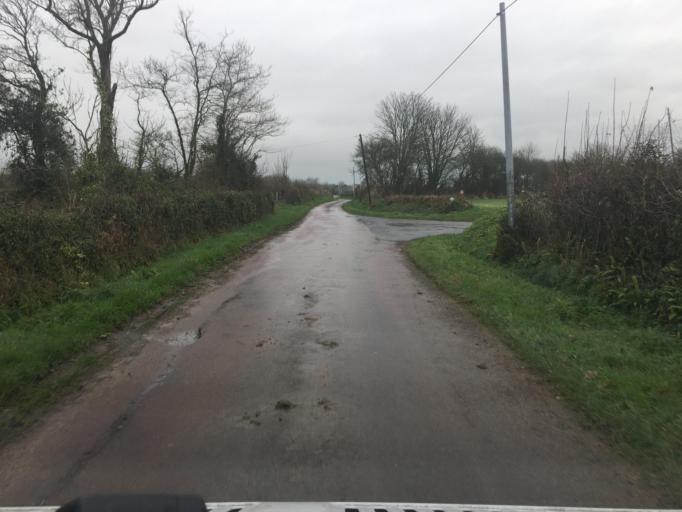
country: FR
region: Lower Normandy
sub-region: Departement de la Manche
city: Sainte-Mere-Eglise
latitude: 49.4303
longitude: -1.2622
